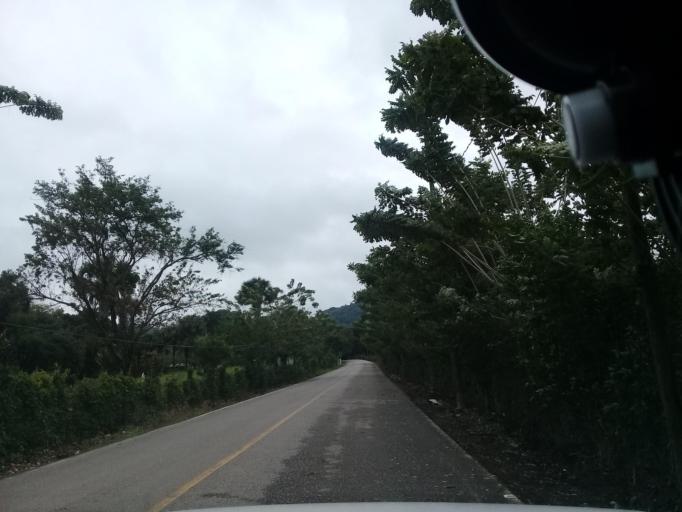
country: MX
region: Veracruz
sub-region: Chalma
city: San Pedro Coyutla
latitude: 21.2196
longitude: -98.4299
